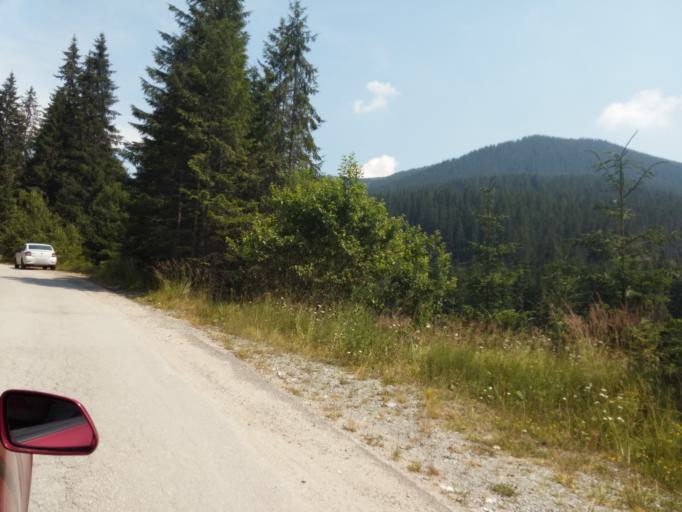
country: RO
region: Valcea
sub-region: Comuna Voineasa
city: Voineasa
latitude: 45.4246
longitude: 23.7660
